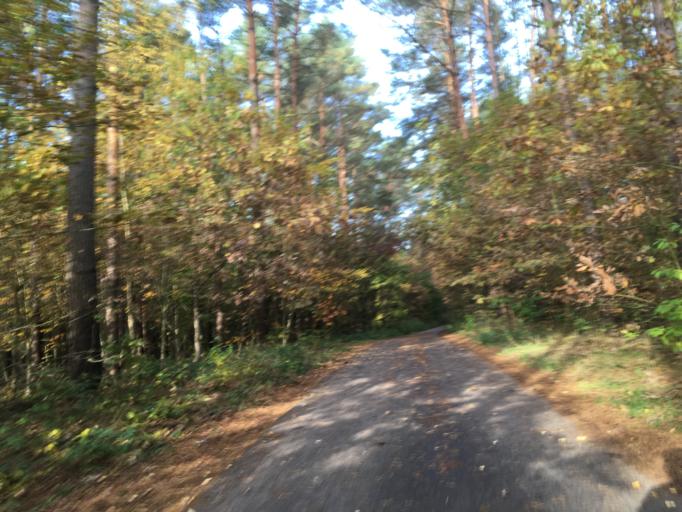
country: DE
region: Brandenburg
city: Wandlitz
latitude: 52.7279
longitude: 13.4633
